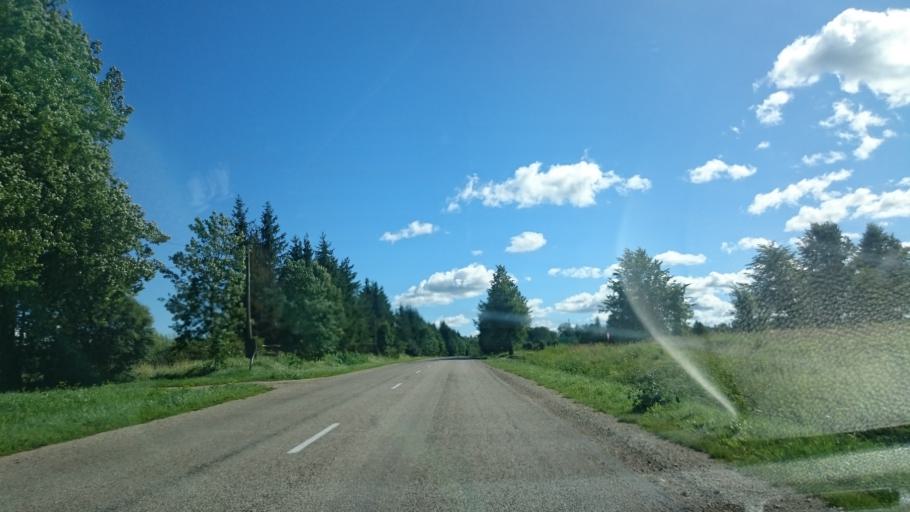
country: LV
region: Aizpute
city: Aizpute
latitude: 56.7417
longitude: 21.6095
